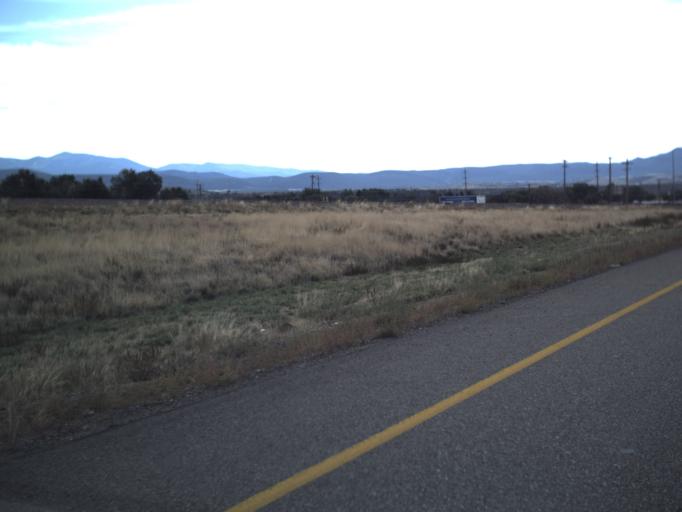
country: US
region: Utah
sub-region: Beaver County
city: Beaver
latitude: 38.2917
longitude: -112.6514
